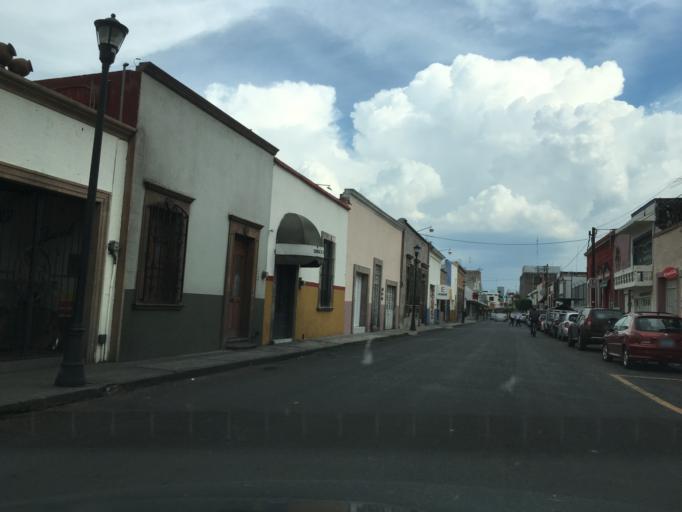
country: MX
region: Guanajuato
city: Celaya
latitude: 20.5247
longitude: -100.8152
